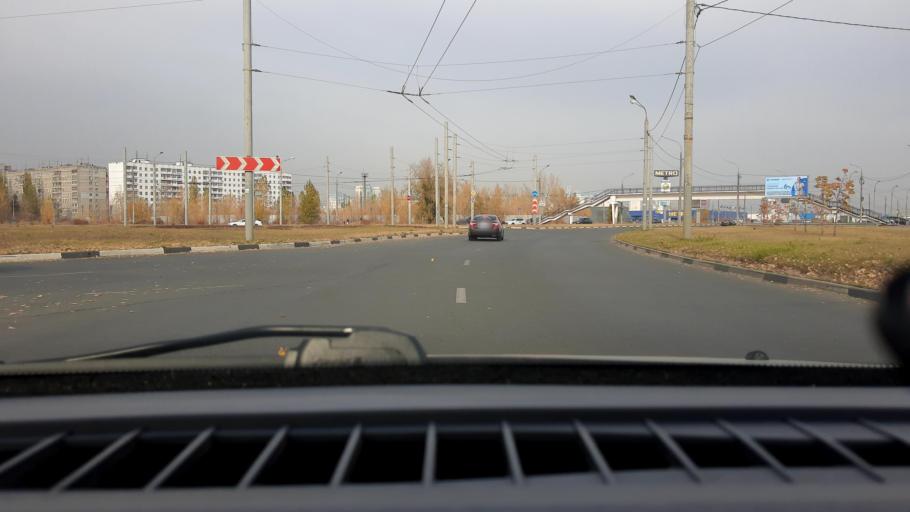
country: RU
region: Nizjnij Novgorod
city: Nizhniy Novgorod
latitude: 56.3292
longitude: 43.9499
